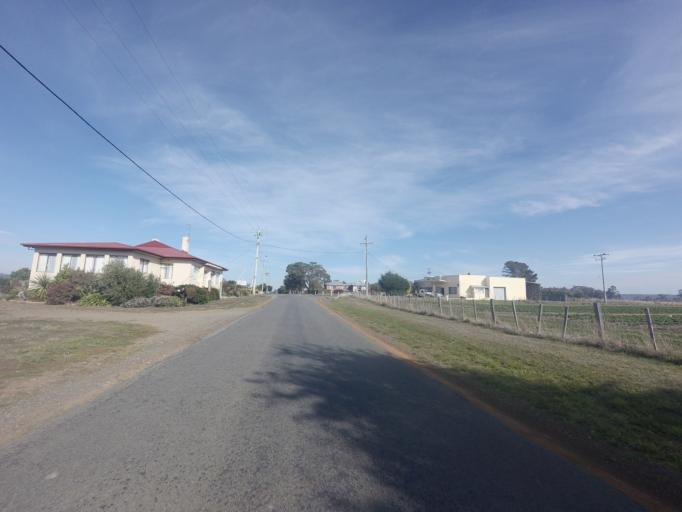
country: AU
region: Tasmania
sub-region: Sorell
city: Sorell
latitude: -42.4529
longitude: 147.4617
